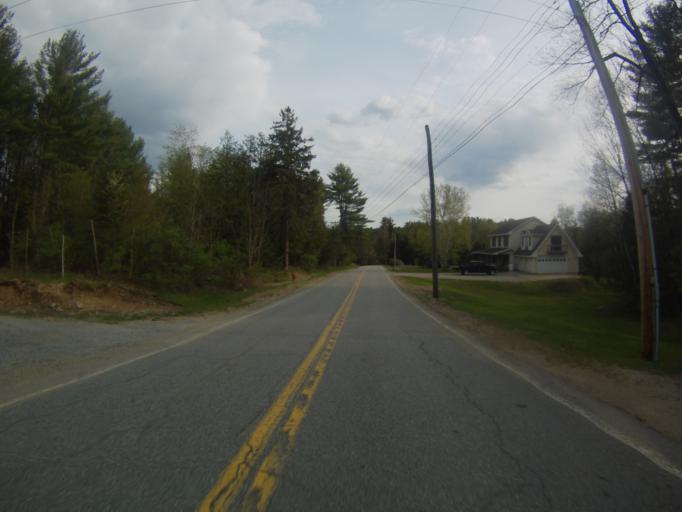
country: US
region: New York
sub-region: Warren County
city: Warrensburg
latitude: 43.7774
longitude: -73.9353
